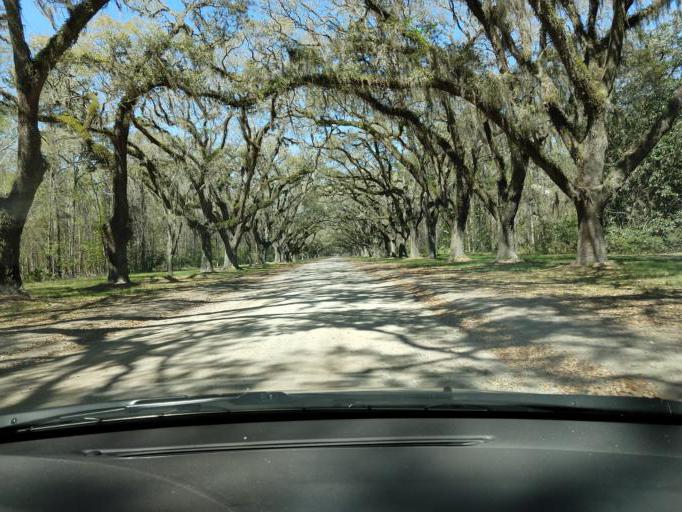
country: US
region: Georgia
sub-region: Chatham County
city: Isle of Hope
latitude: 31.9735
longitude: -81.0692
